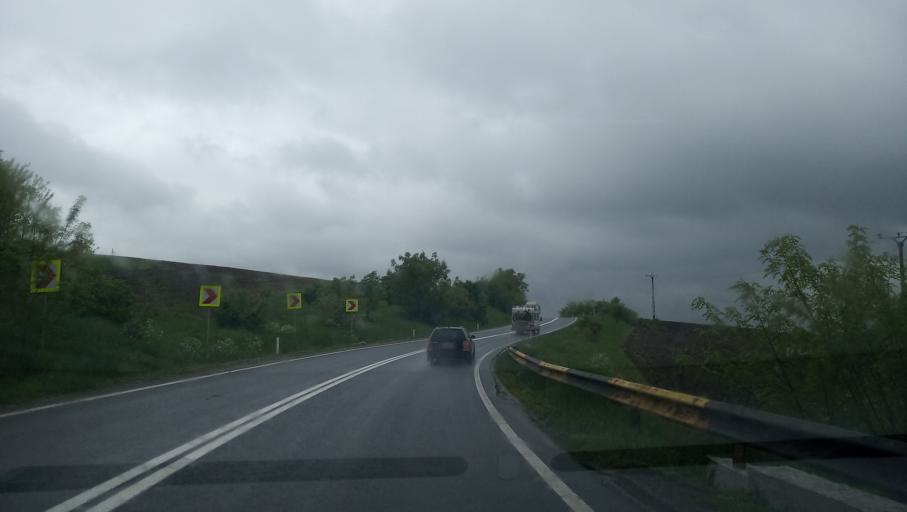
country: RO
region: Alba
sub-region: Comuna Cut
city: Cut
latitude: 45.9200
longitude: 23.6351
